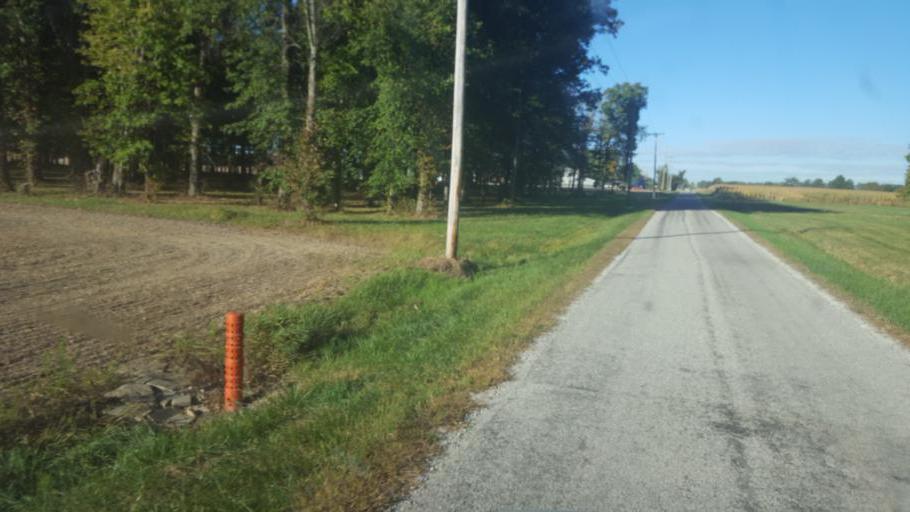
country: US
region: Ohio
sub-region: Crawford County
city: Galion
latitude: 40.6903
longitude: -82.8638
